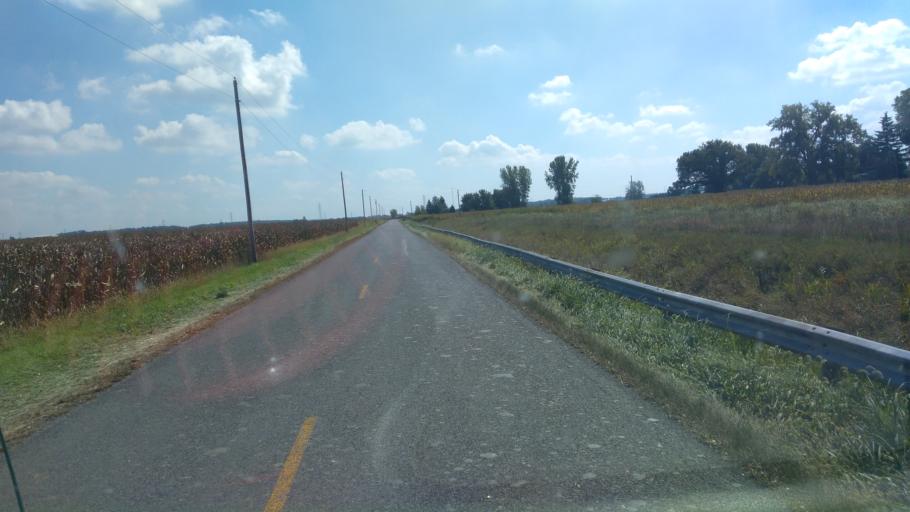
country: US
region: Ohio
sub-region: Hardin County
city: Ada
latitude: 40.6803
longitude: -83.8421
